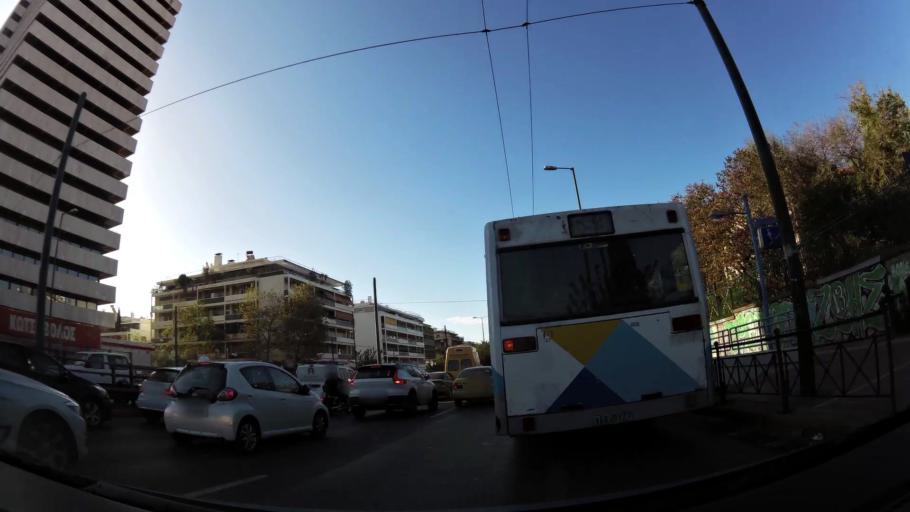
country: GR
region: Attica
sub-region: Nomarchia Athinas
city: Psychiko
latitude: 37.9954
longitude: 23.7685
